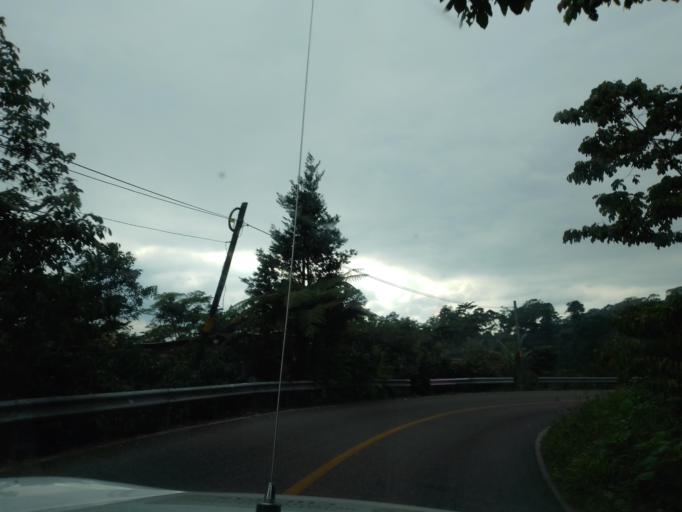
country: MX
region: Chiapas
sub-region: Union Juarez
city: Santo Domingo
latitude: 15.0366
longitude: -92.1245
